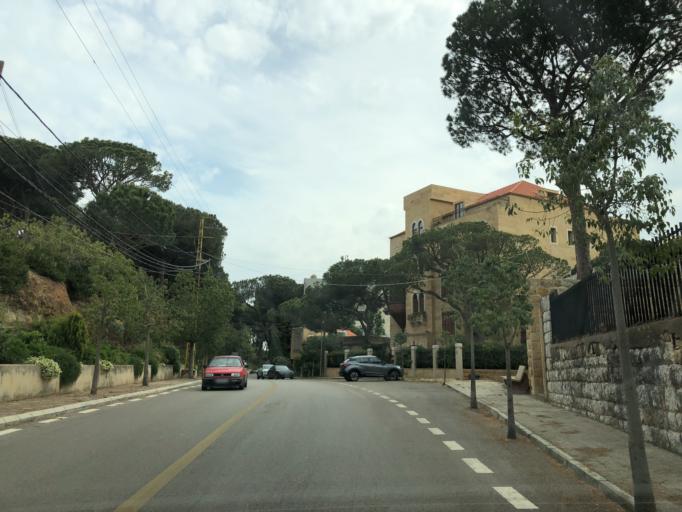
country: LB
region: Mont-Liban
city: Jdaidet el Matn
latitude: 33.8592
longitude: 35.6024
